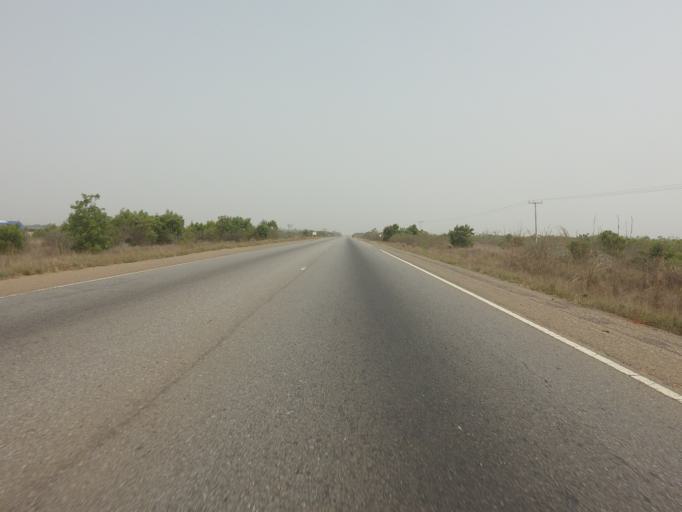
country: GH
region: Greater Accra
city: Tema
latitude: 5.8687
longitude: 0.3114
